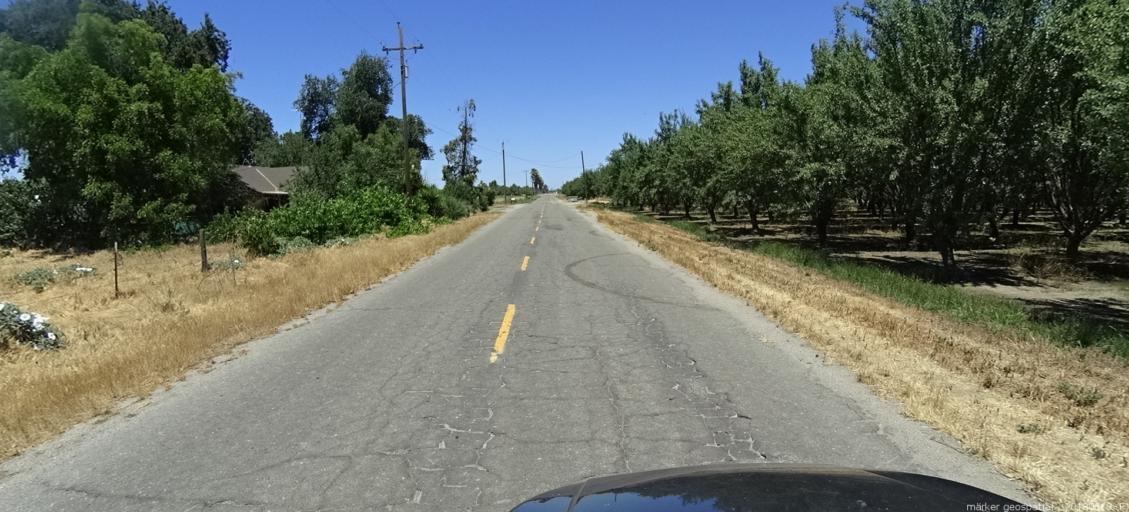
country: US
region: California
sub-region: Madera County
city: Chowchilla
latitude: 37.0588
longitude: -120.2925
